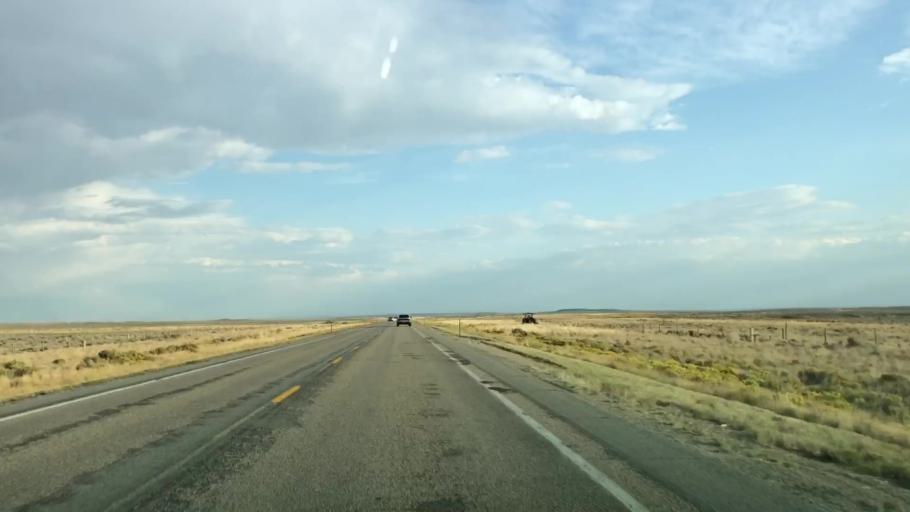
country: US
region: Wyoming
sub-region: Sublette County
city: Pinedale
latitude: 42.4024
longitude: -109.5475
